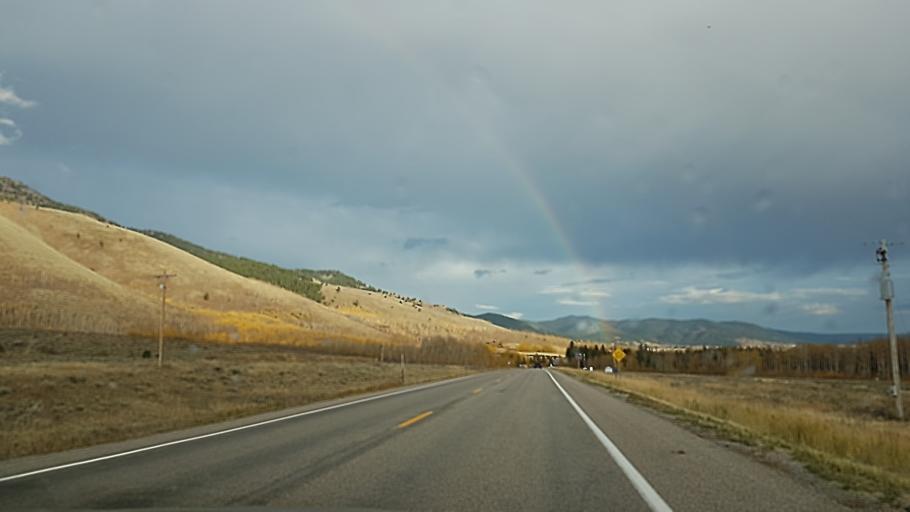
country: US
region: Montana
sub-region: Gallatin County
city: West Yellowstone
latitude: 44.6748
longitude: -111.4136
